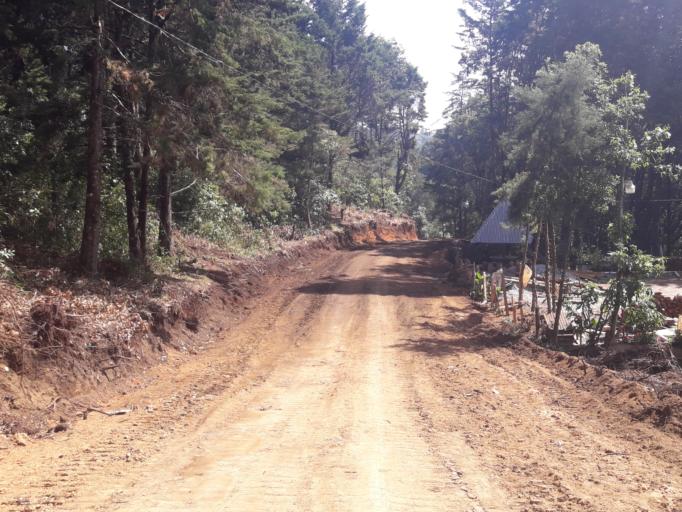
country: GT
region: Quiche
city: Nebaj
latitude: 15.4248
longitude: -91.1373
